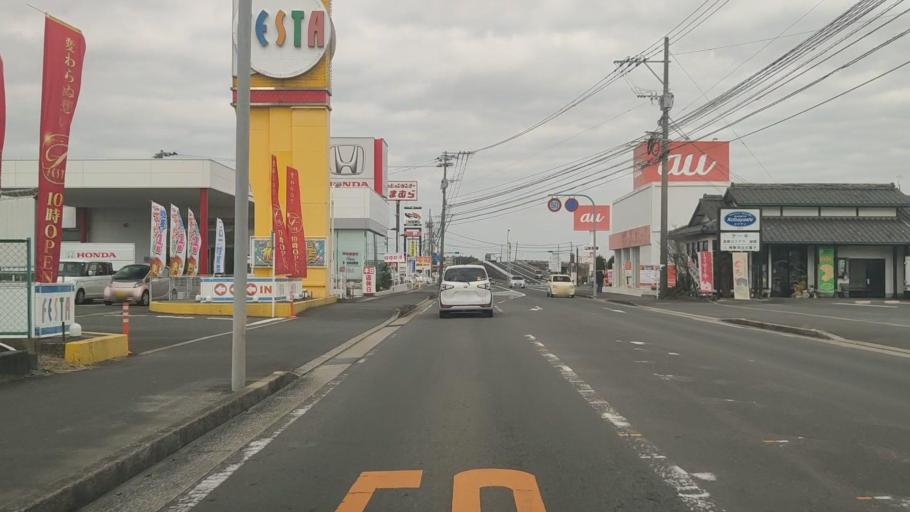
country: JP
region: Nagasaki
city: Shimabara
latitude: 32.8097
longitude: 130.3600
